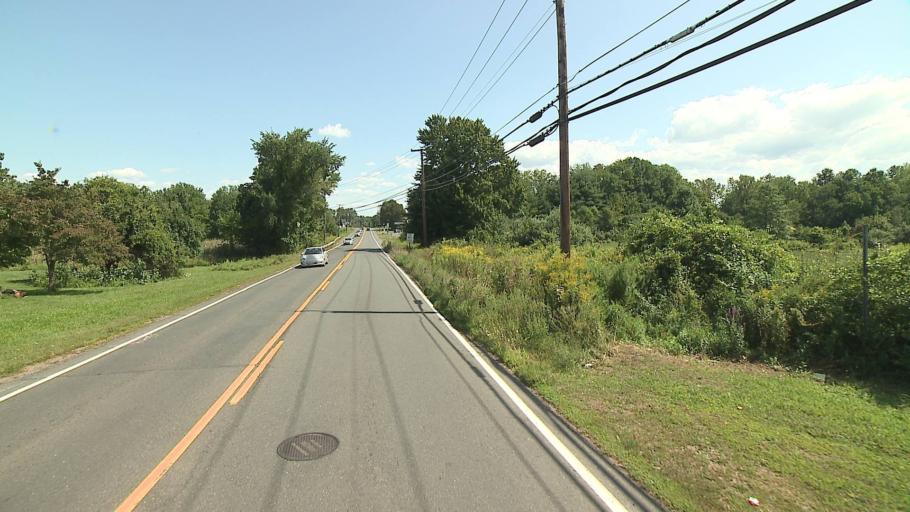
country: US
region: Connecticut
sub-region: Hartford County
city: Southwood Acres
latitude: 41.9348
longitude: -72.5818
